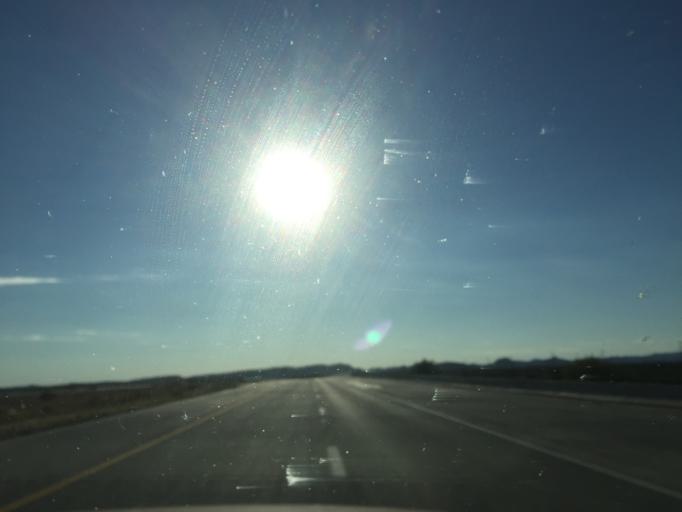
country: US
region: Arizona
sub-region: Maricopa County
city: Anthem
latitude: 33.7790
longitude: -112.2195
